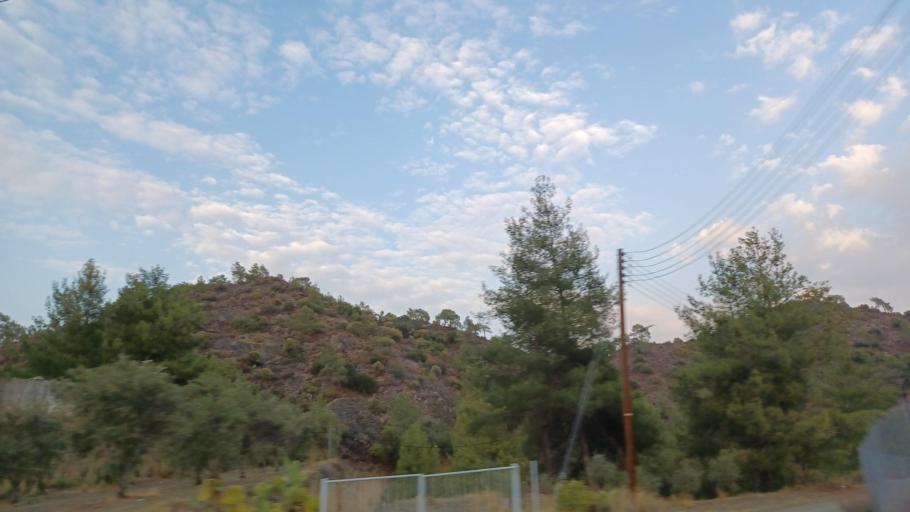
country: CY
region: Limassol
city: Pelendri
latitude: 34.8362
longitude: 32.9570
